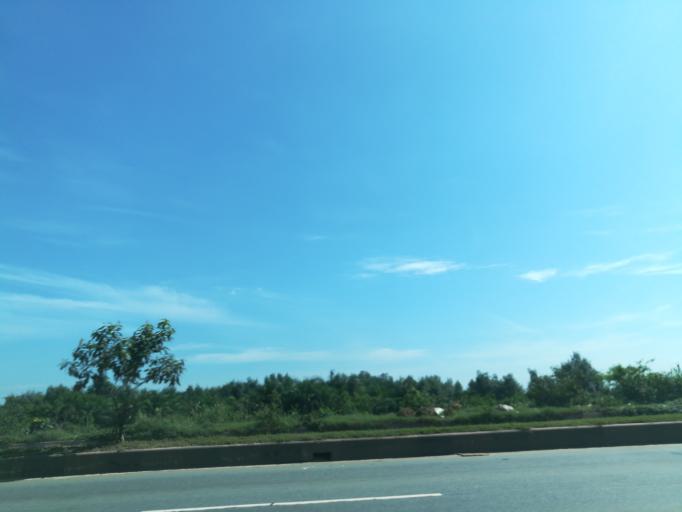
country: NG
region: Lagos
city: Ebute Ikorodu
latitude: 6.6204
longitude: 3.4572
